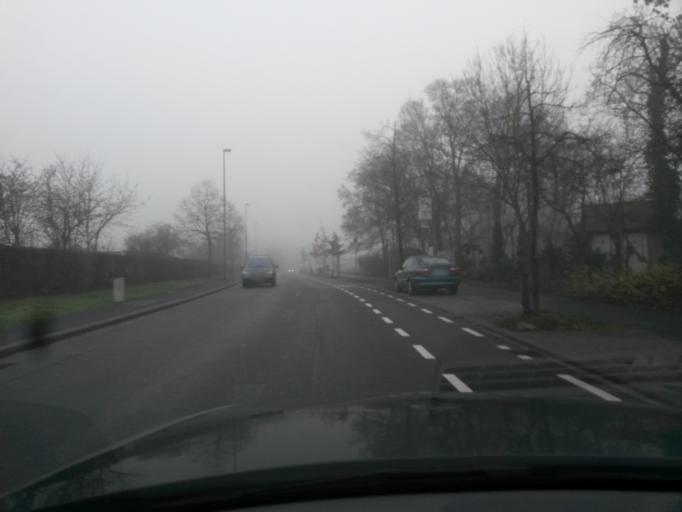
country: DE
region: Bavaria
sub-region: Regierungsbezirk Unterfranken
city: Wuerzburg
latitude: 49.7809
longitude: 9.9628
